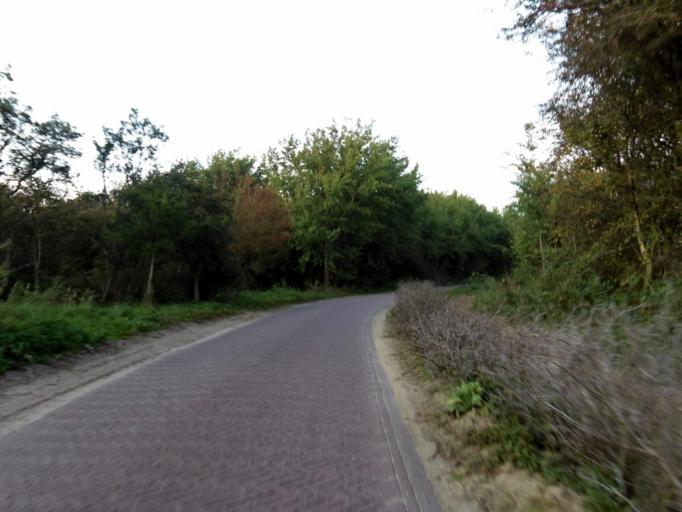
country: NL
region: South Holland
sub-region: Gemeente Wassenaar
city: Wassenaar
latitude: 52.1473
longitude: 4.3463
